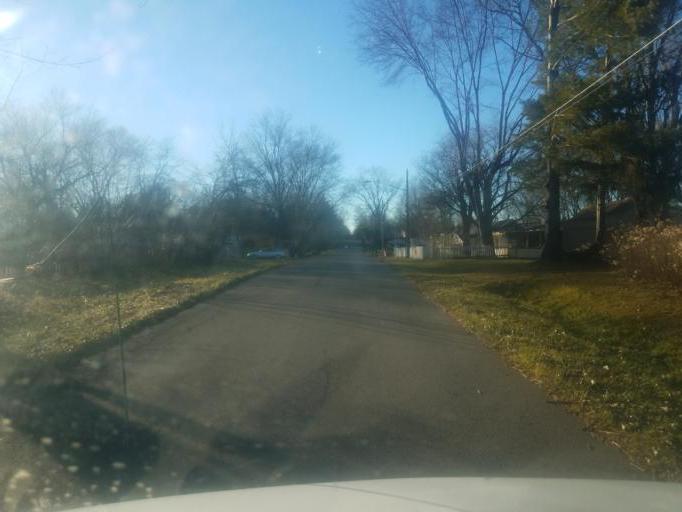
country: US
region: Ohio
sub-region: Richland County
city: Mansfield
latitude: 40.7886
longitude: -82.5303
